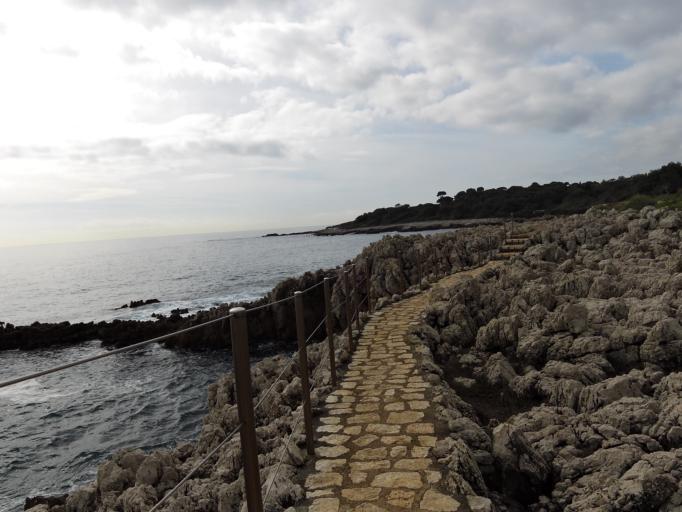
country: FR
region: Provence-Alpes-Cote d'Azur
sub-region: Departement des Alpes-Maritimes
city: Antibes
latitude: 43.5500
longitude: 7.1406
